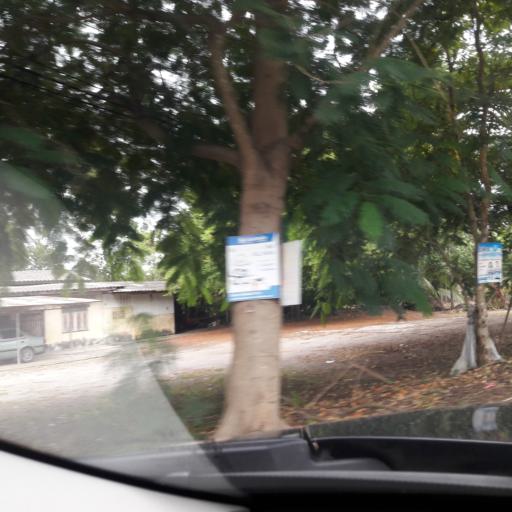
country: TH
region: Ratchaburi
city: Damnoen Saduak
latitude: 13.5629
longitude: 99.9451
